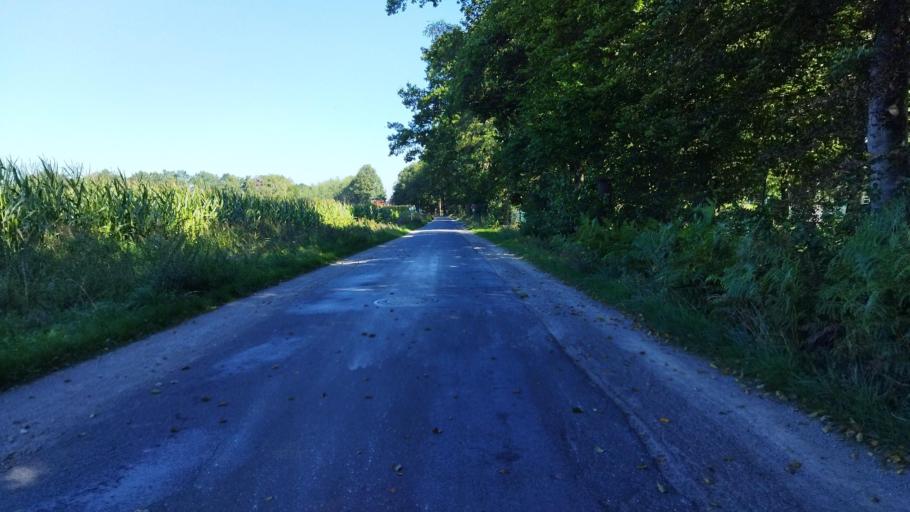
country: DE
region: Lower Saxony
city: Ostercappeln
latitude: 52.3742
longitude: 8.2278
